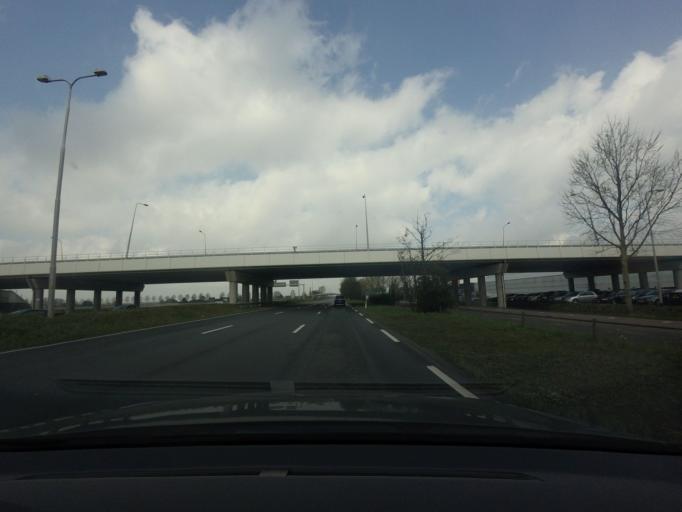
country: NL
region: North Holland
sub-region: Gemeente Aalsmeer
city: Aalsmeer
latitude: 52.2785
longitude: 4.7429
